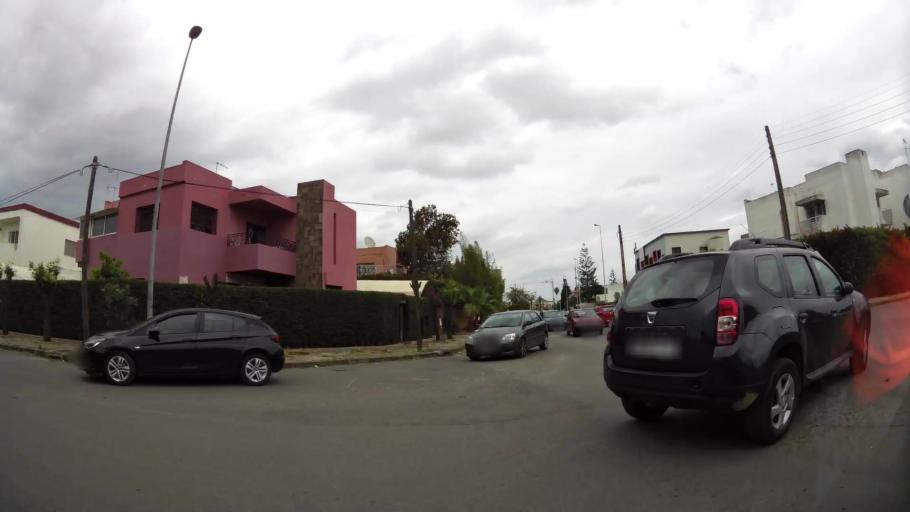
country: MA
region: Grand Casablanca
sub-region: Casablanca
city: Casablanca
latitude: 33.5637
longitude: -7.6407
